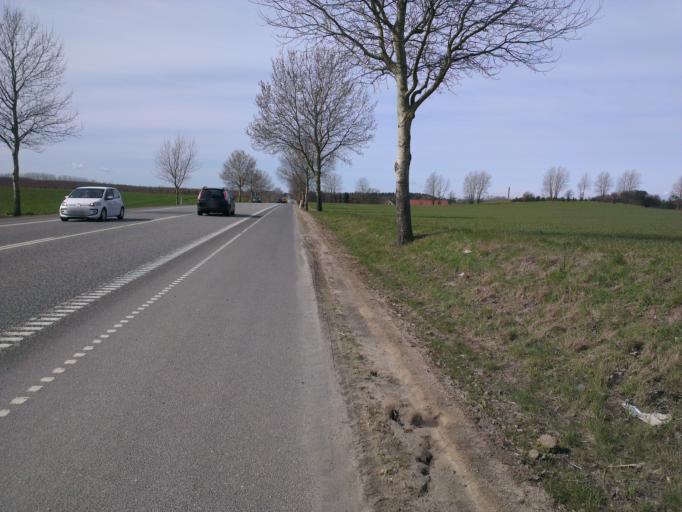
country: DK
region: Capital Region
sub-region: Frederikssund Kommune
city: Frederikssund
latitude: 55.8458
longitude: 12.1071
